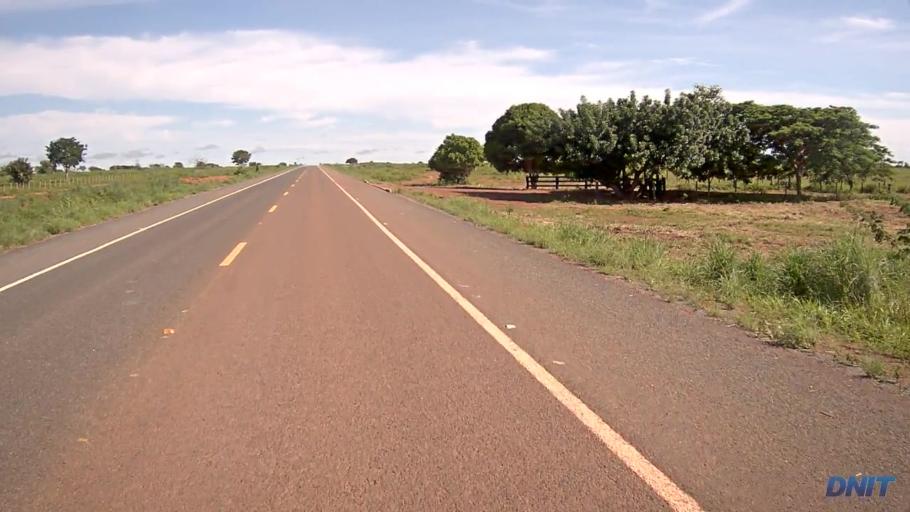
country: BR
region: Goias
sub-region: Sao Miguel Do Araguaia
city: Sao Miguel do Araguaia
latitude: -13.4937
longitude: -50.1082
